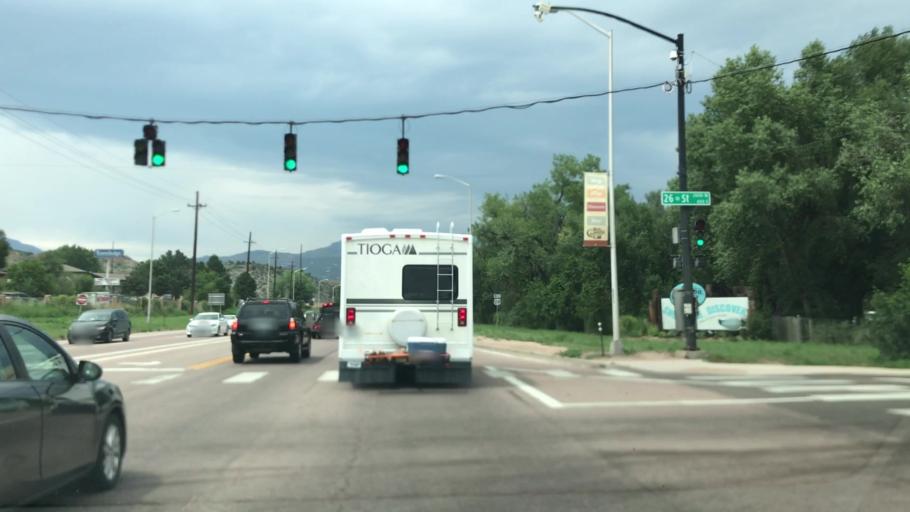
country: US
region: Colorado
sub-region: El Paso County
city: Colorado Springs
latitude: 38.8457
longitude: -104.8665
